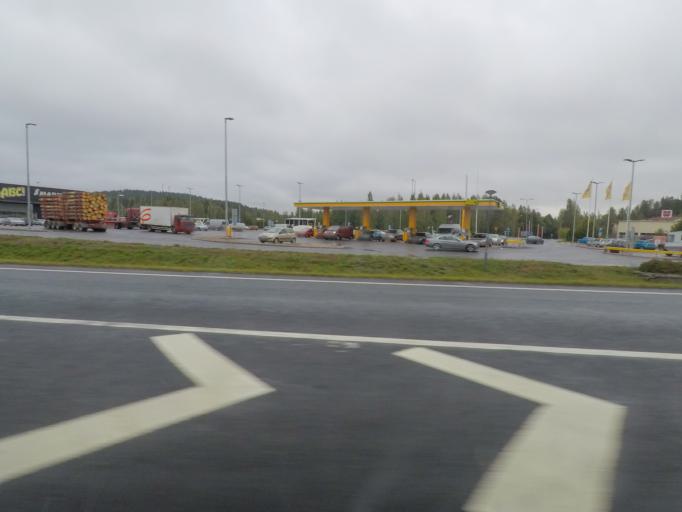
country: FI
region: Northern Savo
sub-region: Kuopio
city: Kuopio
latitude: 62.8370
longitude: 27.6065
